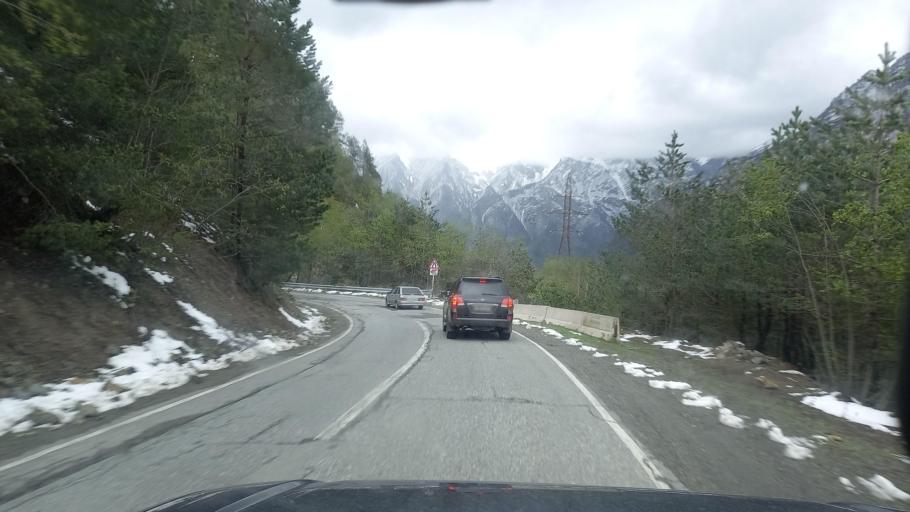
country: RU
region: North Ossetia
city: Mizur
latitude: 42.8030
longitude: 43.9499
